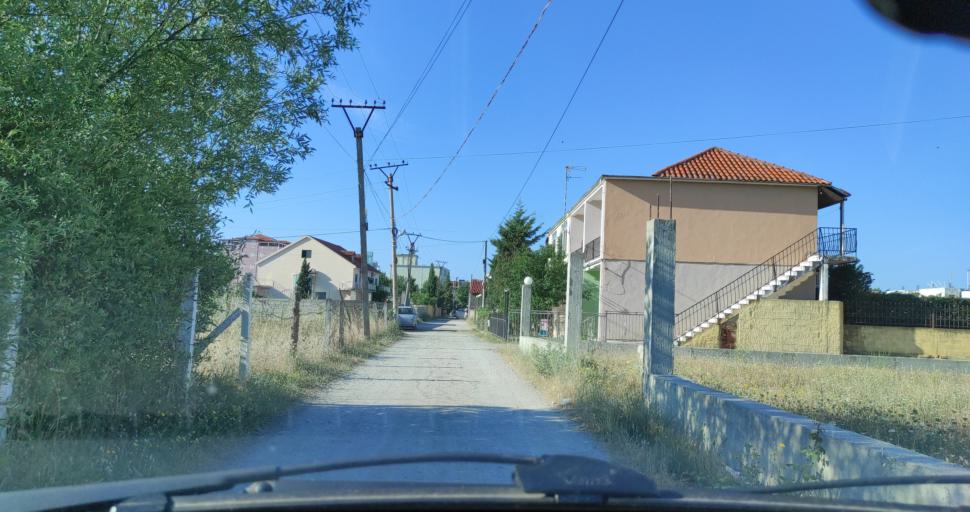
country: AL
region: Shkoder
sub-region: Rrethi i Shkodres
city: Velipoje
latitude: 41.8676
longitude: 19.4261
